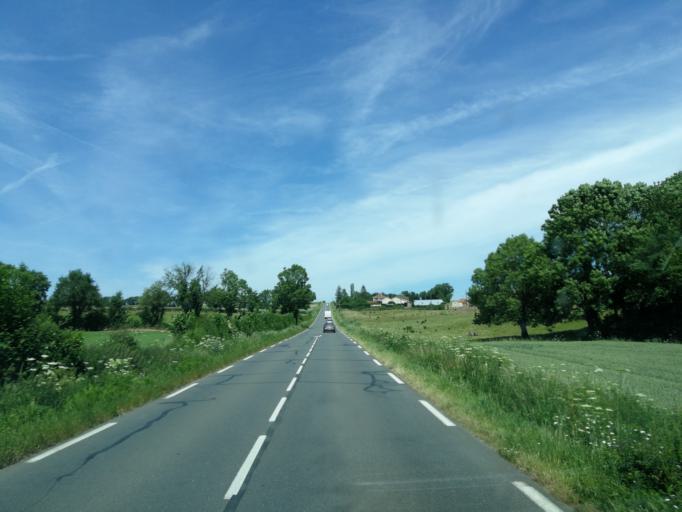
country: FR
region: Pays de la Loire
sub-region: Departement de la Vendee
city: La Tardiere
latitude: 46.6726
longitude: -0.7208
